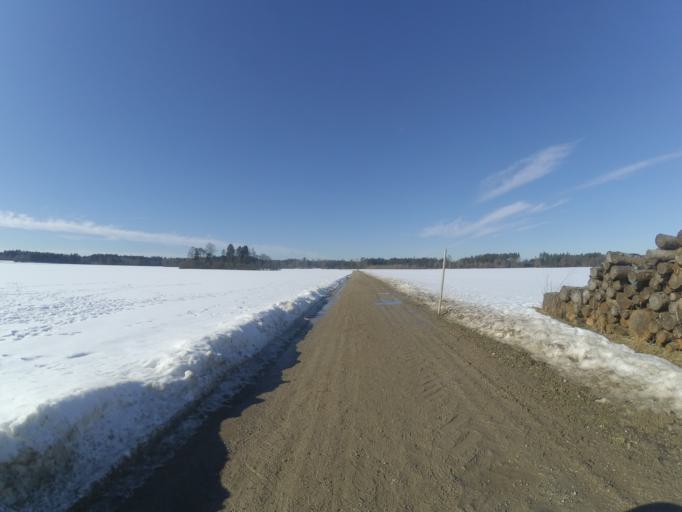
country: DE
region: Bavaria
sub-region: Upper Bavaria
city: Aying
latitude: 47.9775
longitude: 11.7663
